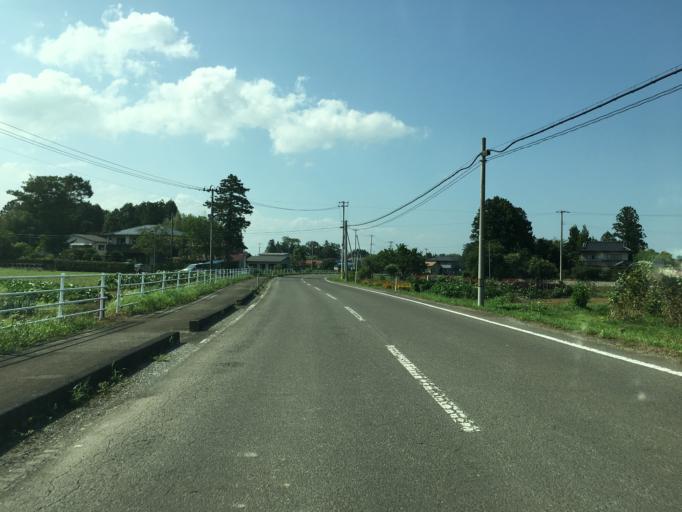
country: JP
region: Miyagi
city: Kakuda
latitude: 37.9475
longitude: 140.7978
